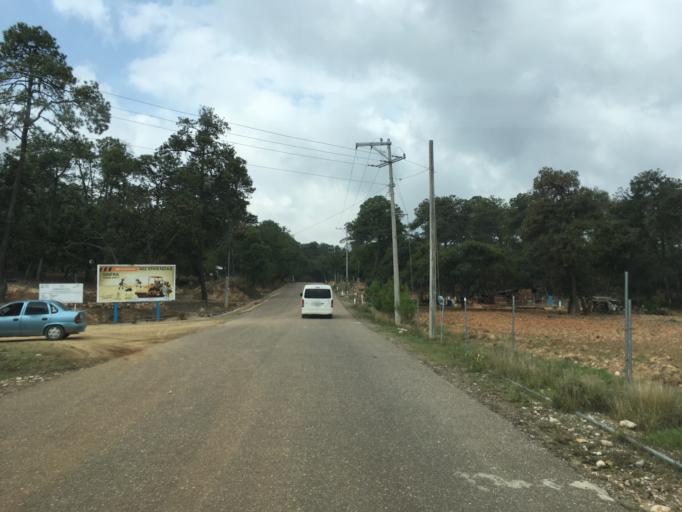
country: MX
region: Oaxaca
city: Santiago Tilantongo
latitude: 17.2172
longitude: -97.2786
